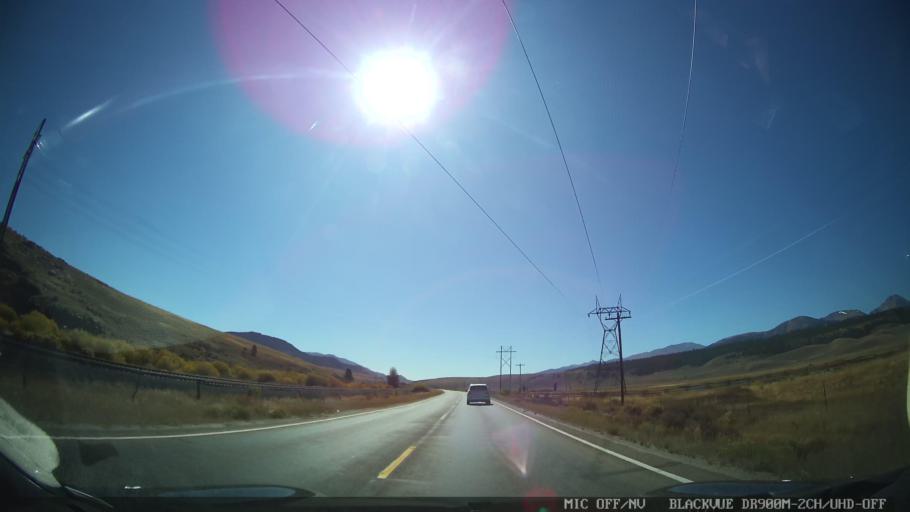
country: US
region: Colorado
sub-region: Lake County
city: Leadville
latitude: 39.1254
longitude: -106.3124
